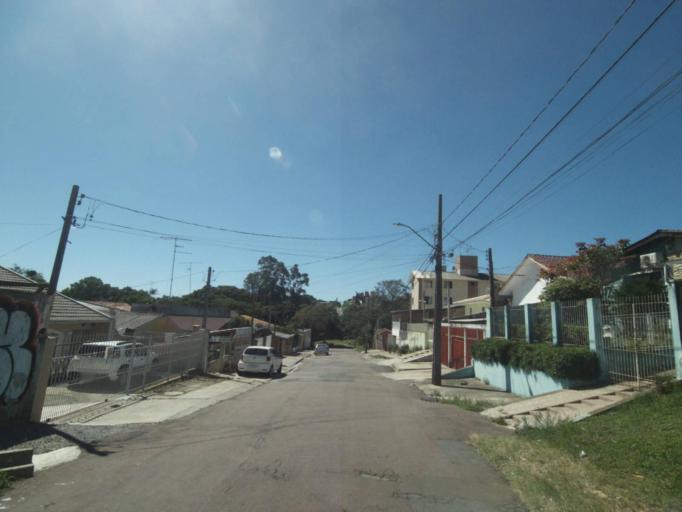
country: BR
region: Parana
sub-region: Curitiba
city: Curitiba
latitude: -25.4581
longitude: -49.3516
